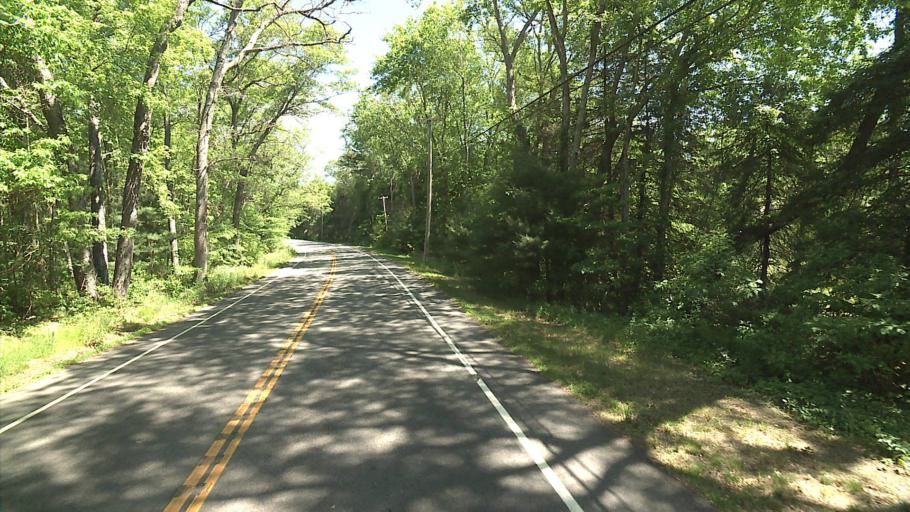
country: US
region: Rhode Island
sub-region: Washington County
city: Hopkinton
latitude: 41.5297
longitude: -71.8366
